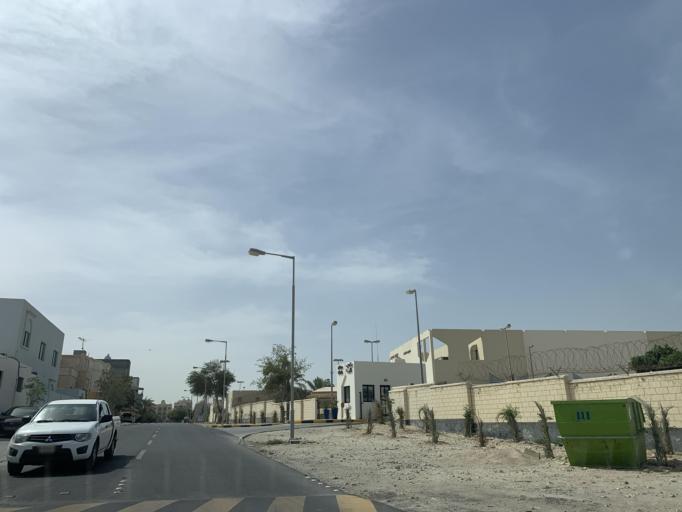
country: BH
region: Northern
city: Ar Rifa'
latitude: 26.1422
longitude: 50.5753
